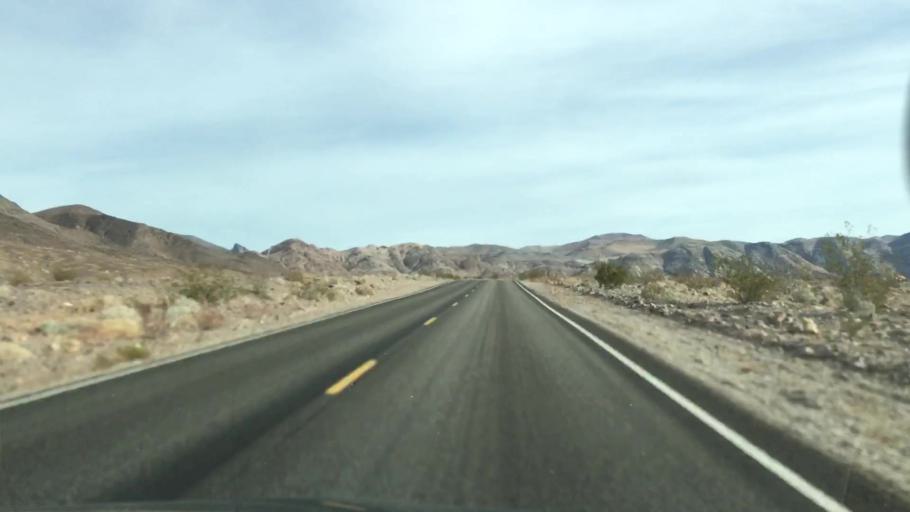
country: US
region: Nevada
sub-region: Nye County
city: Beatty
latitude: 36.7090
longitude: -116.9882
